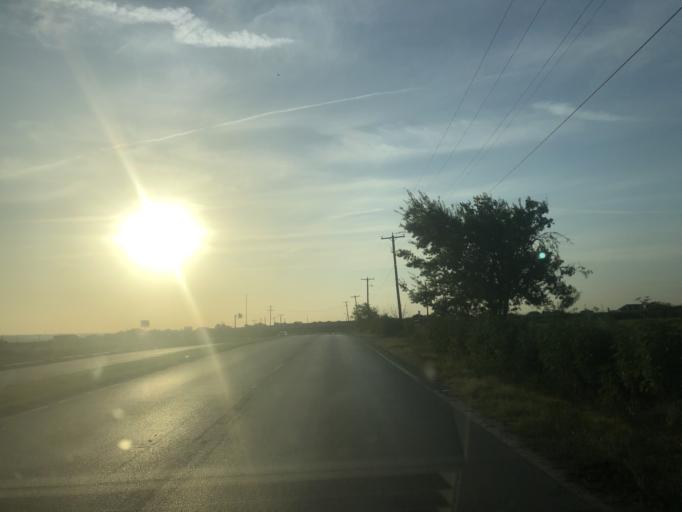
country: US
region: Texas
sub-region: Tarrant County
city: White Settlement
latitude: 32.7744
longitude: -97.4785
